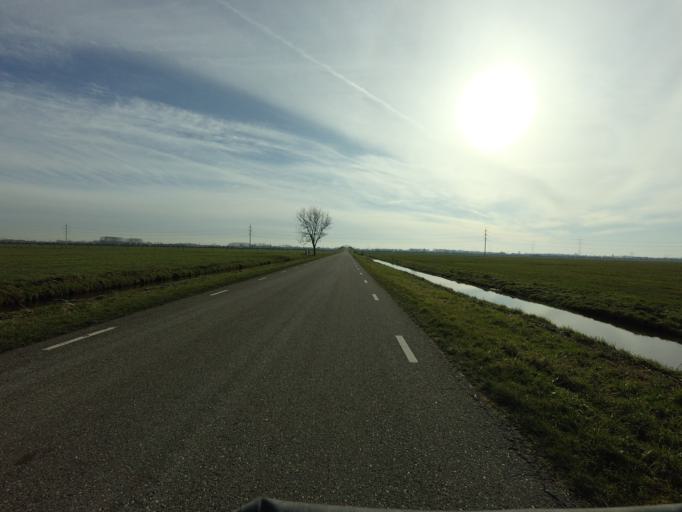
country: NL
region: South Holland
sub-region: Gemeente Hardinxveld-Giessendam
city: Neder-Hardinxveld
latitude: 51.8415
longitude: 4.8242
